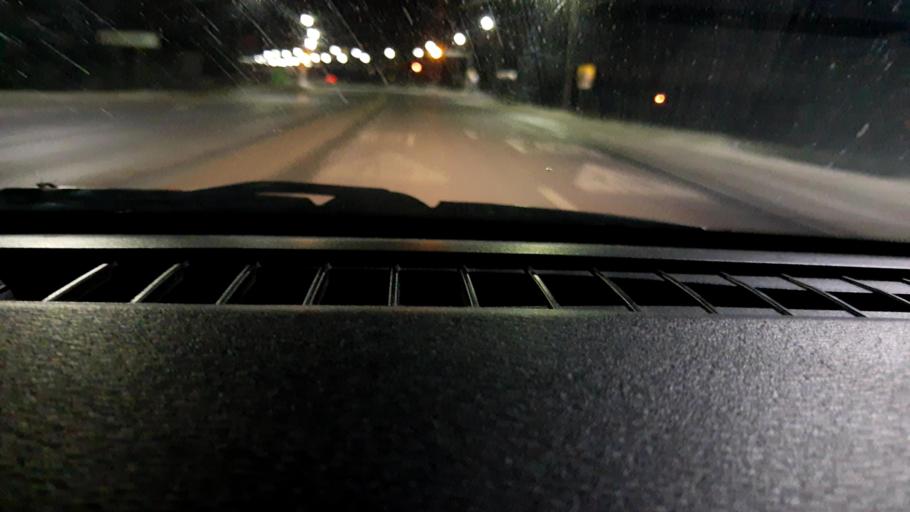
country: RU
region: Nizjnij Novgorod
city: Sitniki
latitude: 56.5082
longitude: 44.0234
